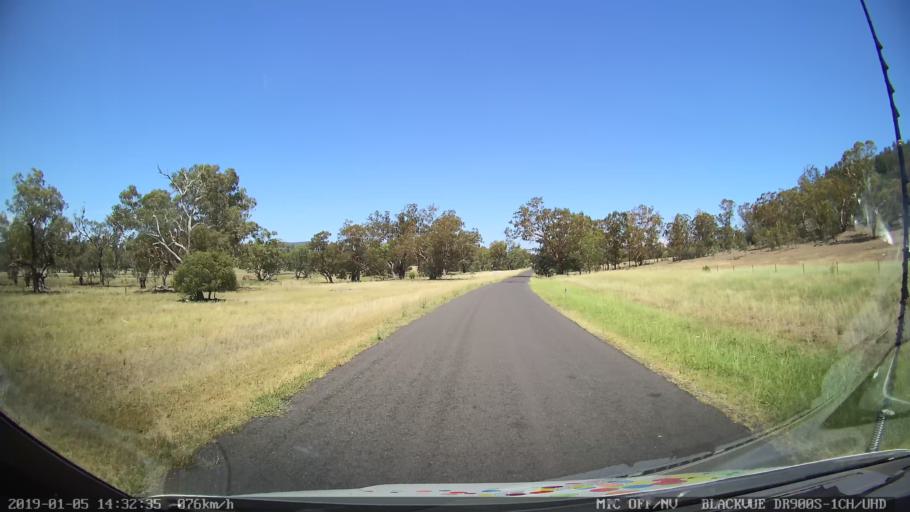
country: AU
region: New South Wales
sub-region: Tamworth Municipality
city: Phillip
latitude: -31.2211
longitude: 150.6202
